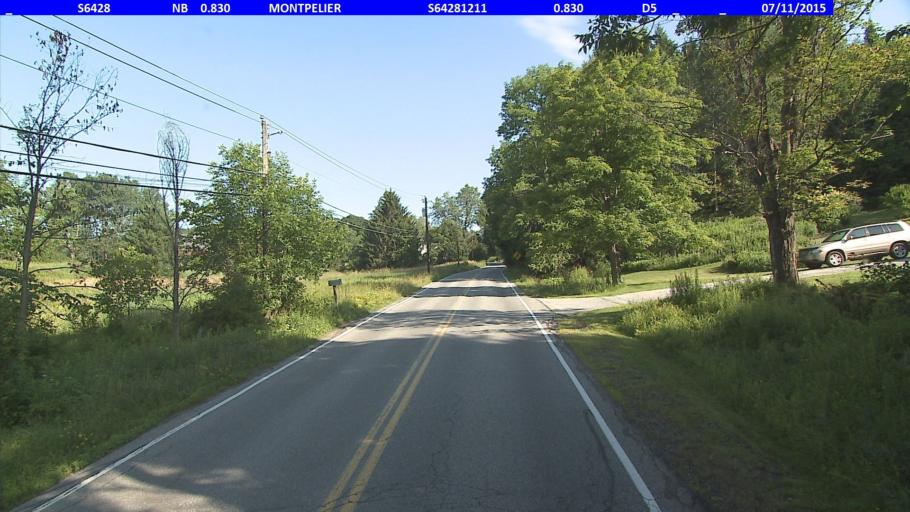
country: US
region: Vermont
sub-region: Washington County
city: Montpelier
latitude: 44.2737
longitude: -72.5921
